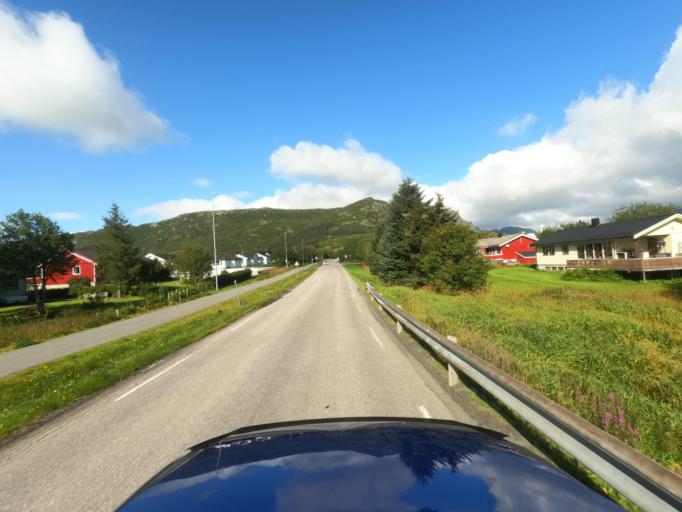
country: NO
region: Nordland
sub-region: Vestvagoy
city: Evjen
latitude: 68.1391
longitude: 13.8360
